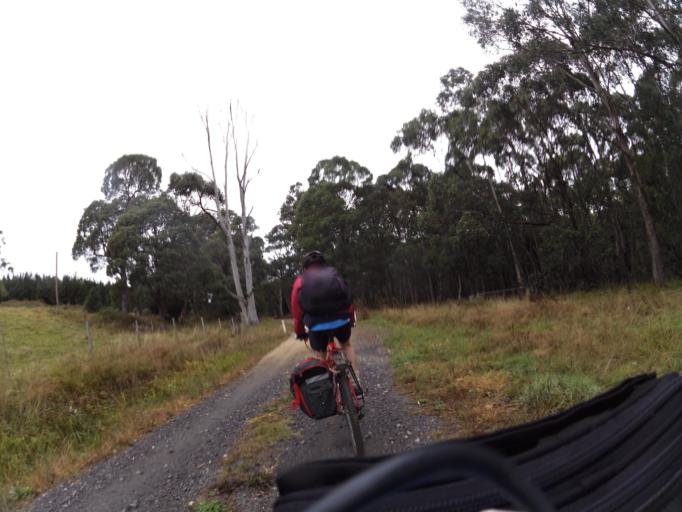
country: AU
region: New South Wales
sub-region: Greater Hume Shire
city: Holbrook
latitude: -36.1675
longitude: 147.4955
